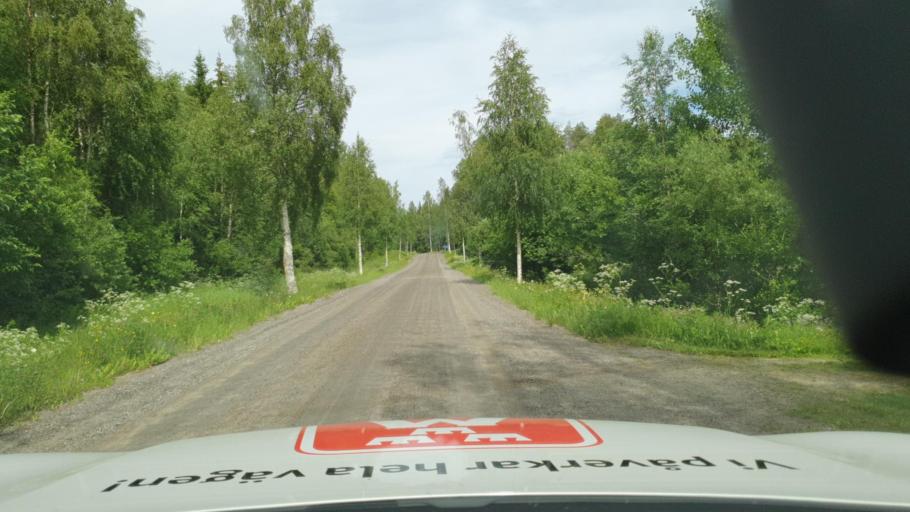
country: SE
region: Vaesterbotten
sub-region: Skelleftea Kommun
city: Burtraesk
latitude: 64.4728
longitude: 20.4791
